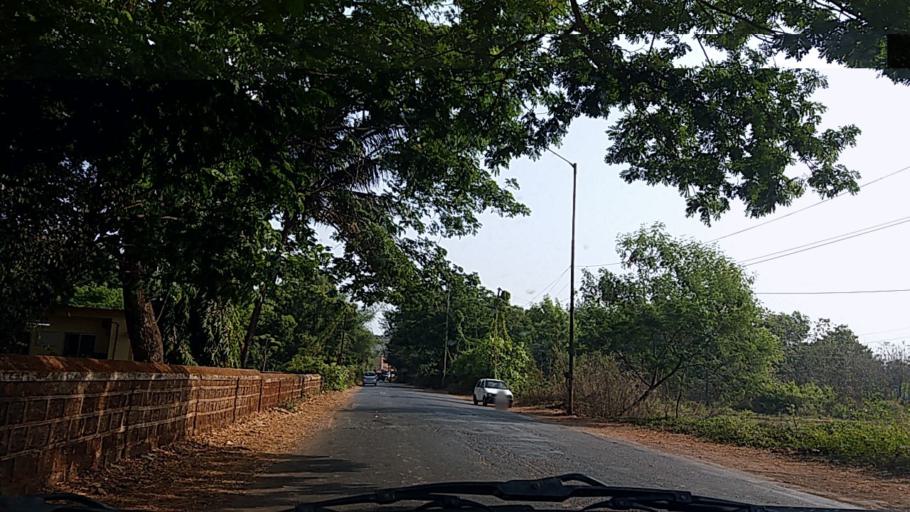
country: IN
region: Goa
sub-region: South Goa
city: Madgaon
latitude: 15.2643
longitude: 73.9701
